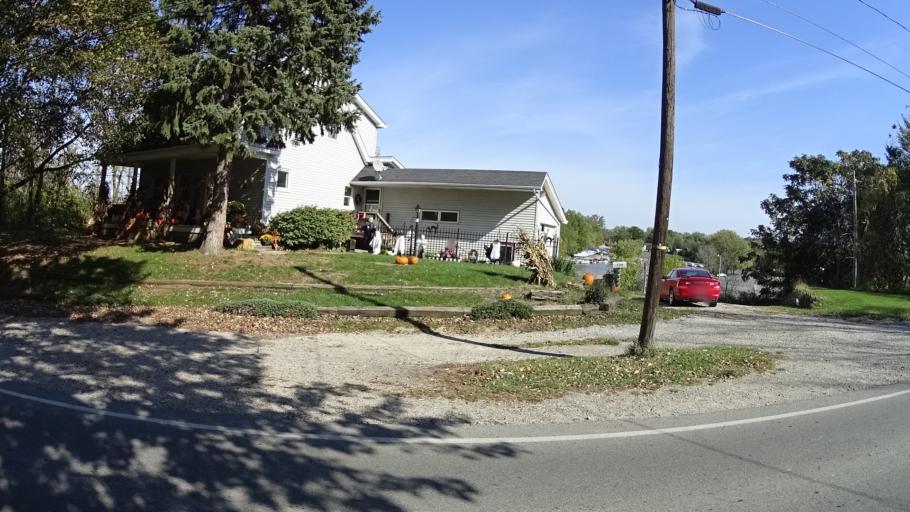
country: US
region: Ohio
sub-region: Lorain County
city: Vermilion
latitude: 41.4204
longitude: -82.3581
